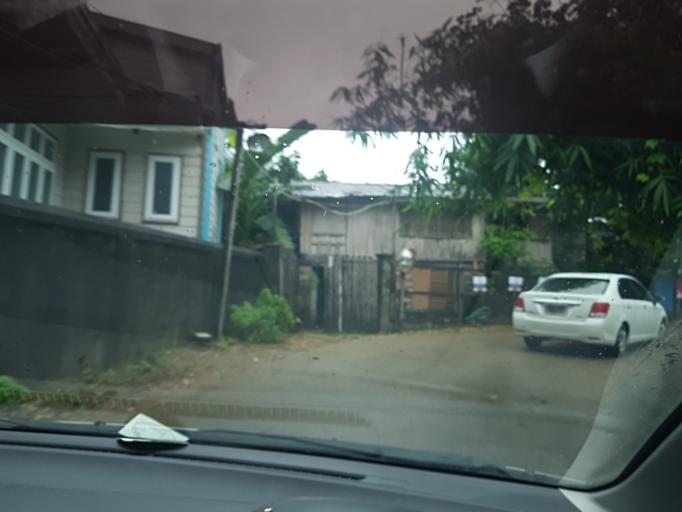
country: MM
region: Yangon
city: Yangon
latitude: 16.8127
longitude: 96.1517
